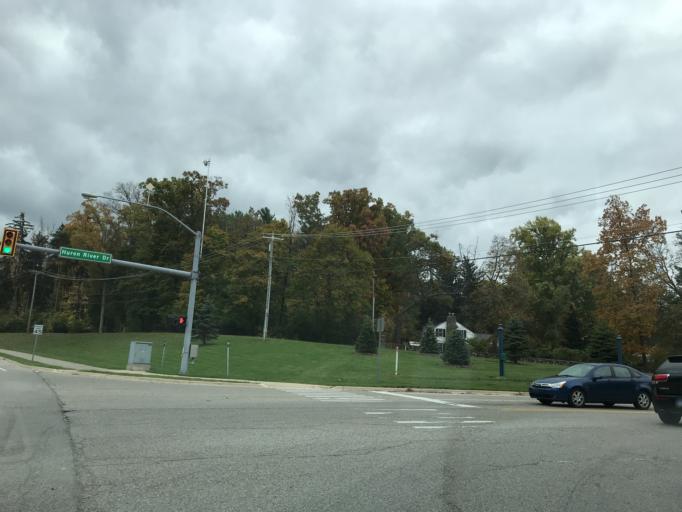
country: US
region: Michigan
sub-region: Washtenaw County
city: Ypsilanti
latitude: 42.2685
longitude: -83.6698
